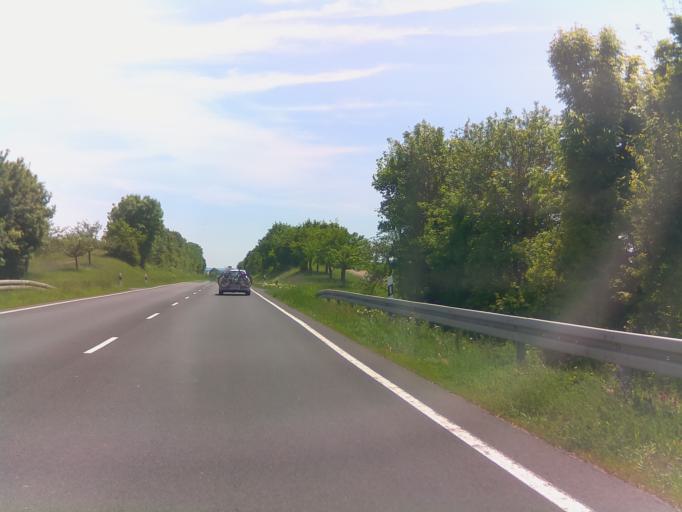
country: DE
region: Bavaria
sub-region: Regierungsbezirk Unterfranken
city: Oerlenbach
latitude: 50.1583
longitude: 10.1486
